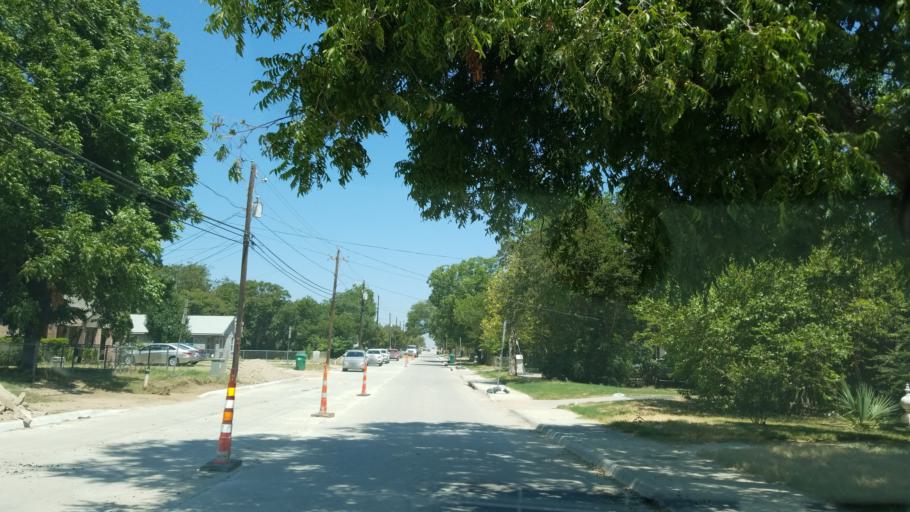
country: US
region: Texas
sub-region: Dallas County
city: Cockrell Hill
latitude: 32.7399
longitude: -96.8914
